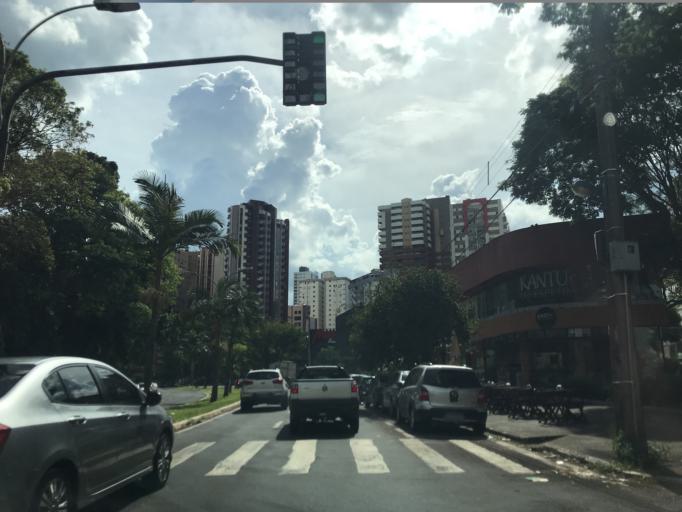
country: BR
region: Parana
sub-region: Maringa
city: Maringa
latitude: -23.4229
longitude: -51.9312
